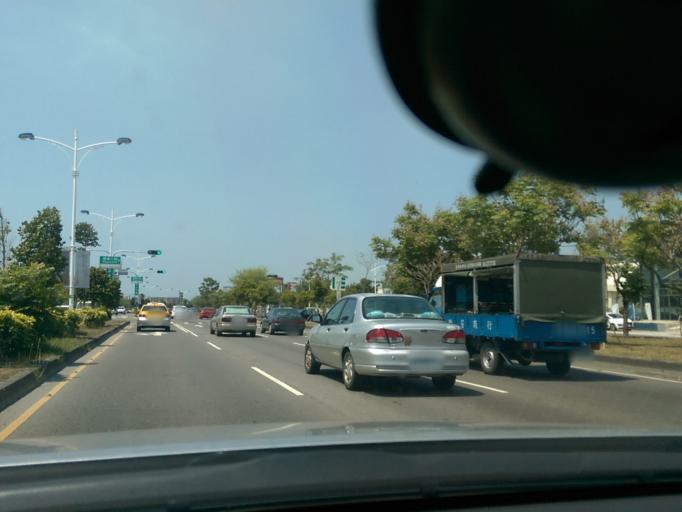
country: TW
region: Taiwan
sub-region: Chiayi
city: Jiayi Shi
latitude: 23.5030
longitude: 120.4486
